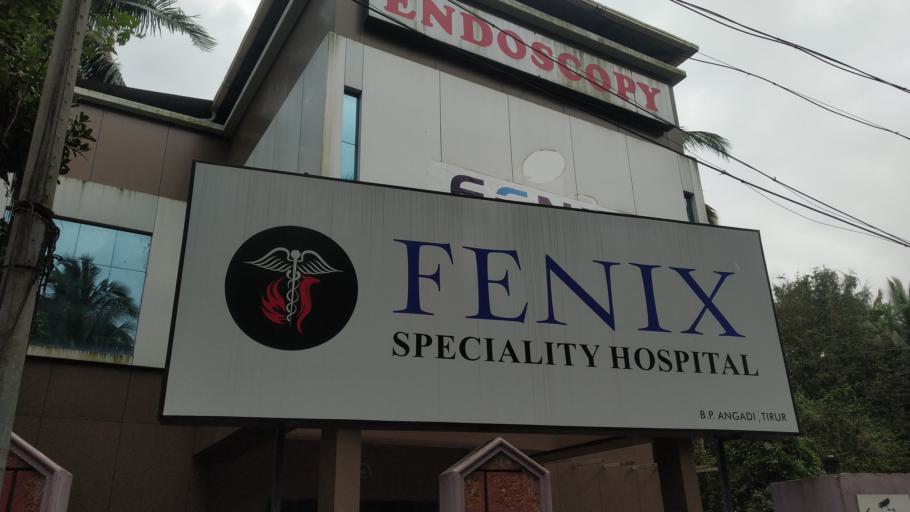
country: IN
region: Kerala
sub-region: Malappuram
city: Tirur
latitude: 10.8841
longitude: 75.9337
